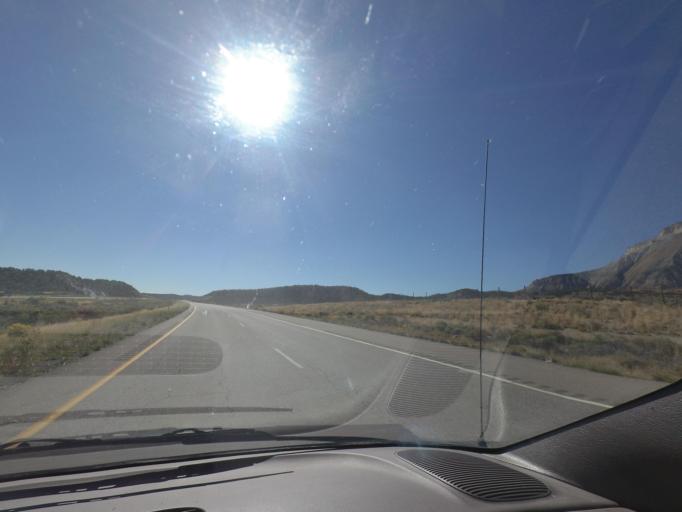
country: US
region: Colorado
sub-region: Garfield County
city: Parachute
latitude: 39.3830
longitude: -108.1507
